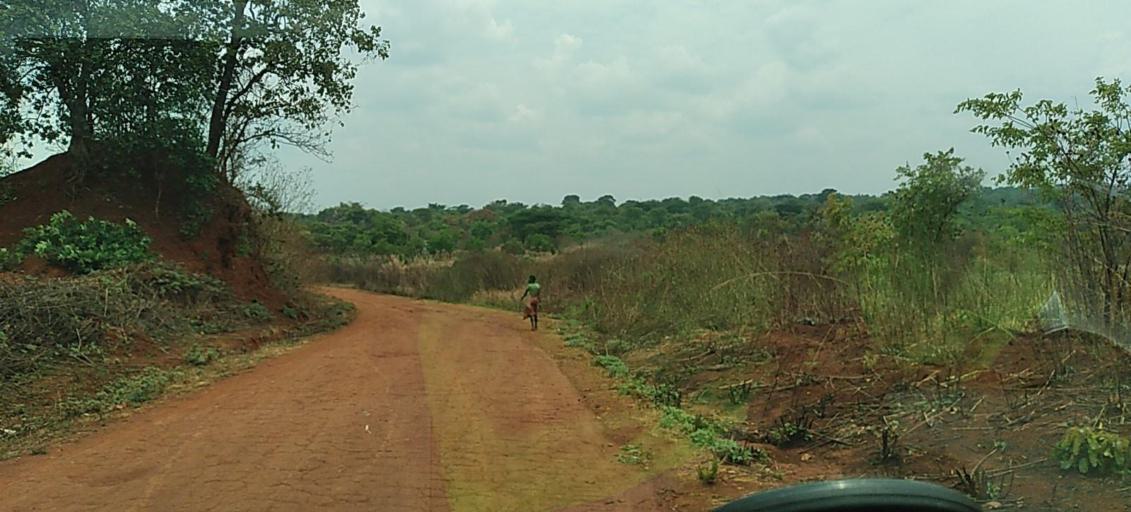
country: ZM
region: North-Western
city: Kansanshi
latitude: -12.0438
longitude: 26.3900
